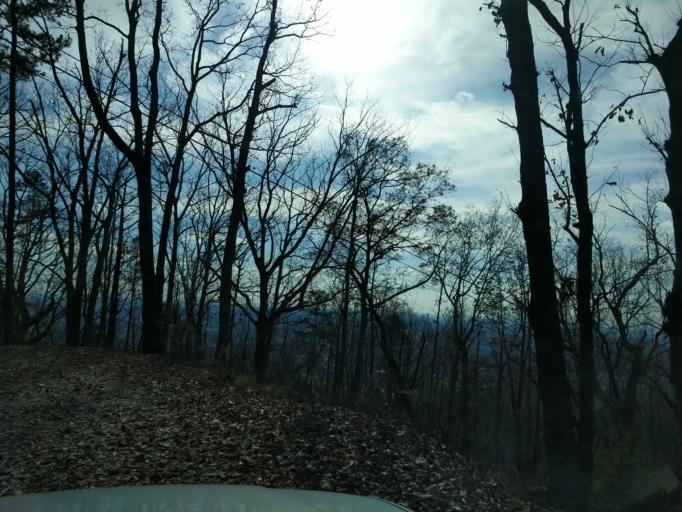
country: US
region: South Carolina
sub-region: Pickens County
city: Pickens
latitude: 34.8330
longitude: -82.8043
